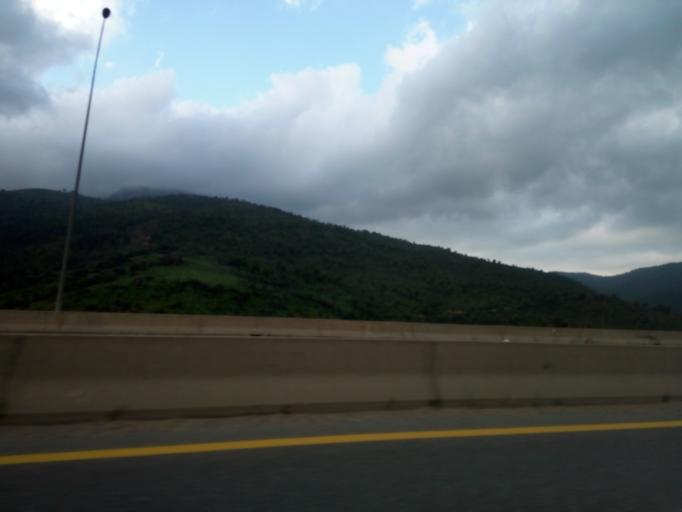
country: DZ
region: Boumerdes
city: Arbatache
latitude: 36.5796
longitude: 3.4482
